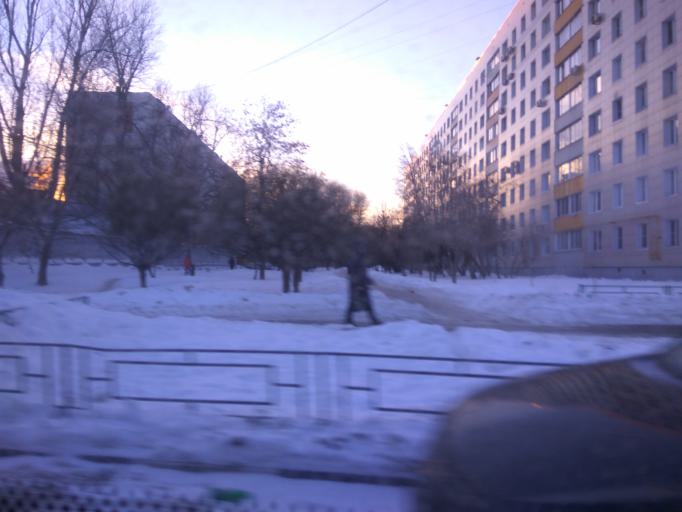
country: RU
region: Moscow
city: Biryulevo
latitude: 55.5919
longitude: 37.6637
